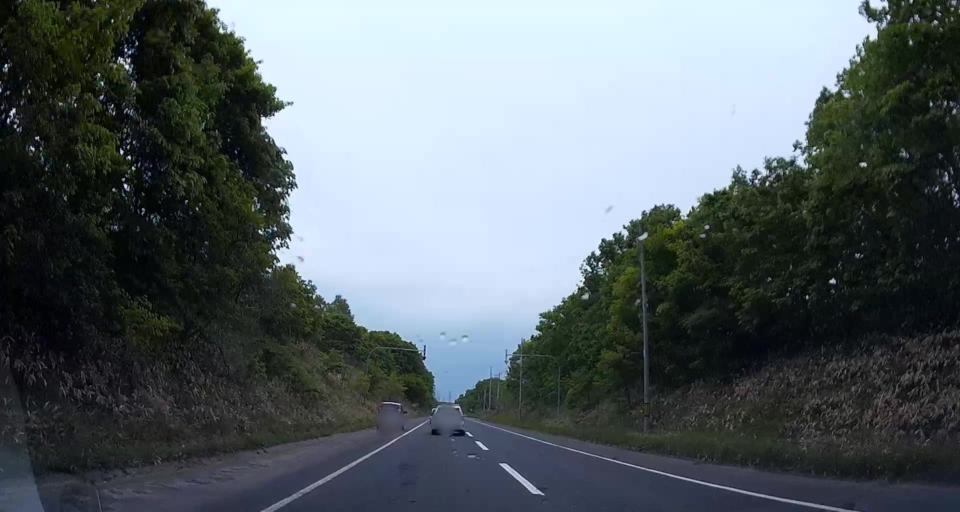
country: JP
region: Hokkaido
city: Chitose
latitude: 42.7046
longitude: 141.7436
